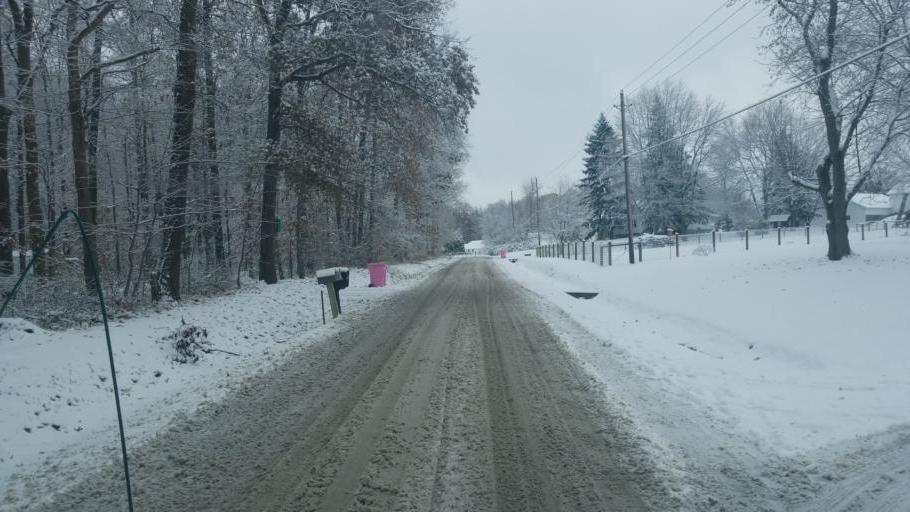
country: US
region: Ohio
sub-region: Geauga County
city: Middlefield
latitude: 41.4251
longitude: -81.0494
